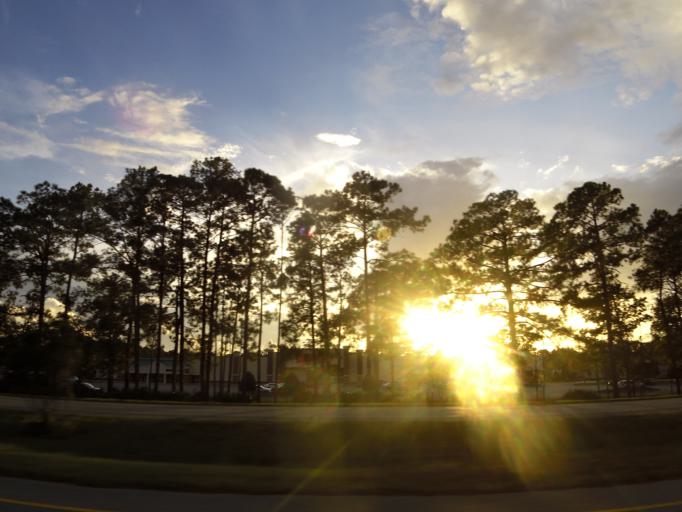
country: US
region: Georgia
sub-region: Glynn County
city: Country Club Estates
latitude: 31.2163
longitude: -81.4919
